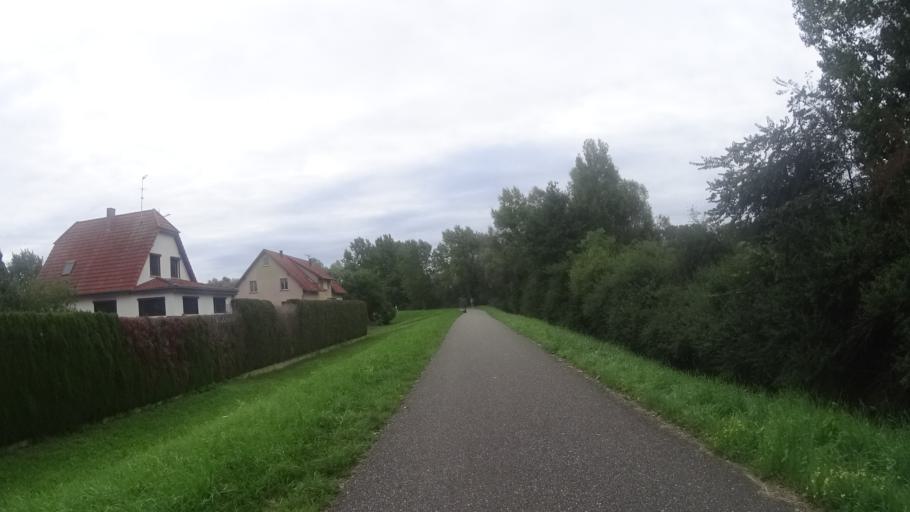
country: DE
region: Baden-Wuerttemberg
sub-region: Karlsruhe Region
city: Steinmauern
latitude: 48.9178
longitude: 8.1518
